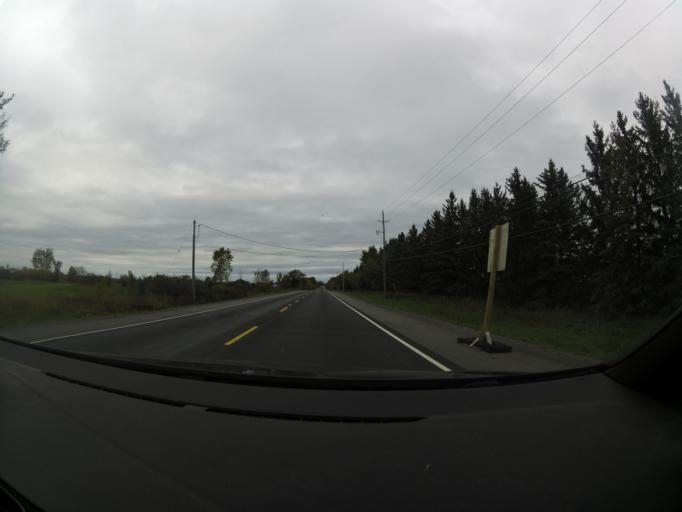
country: CA
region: Ontario
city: Bells Corners
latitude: 45.4086
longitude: -76.0041
